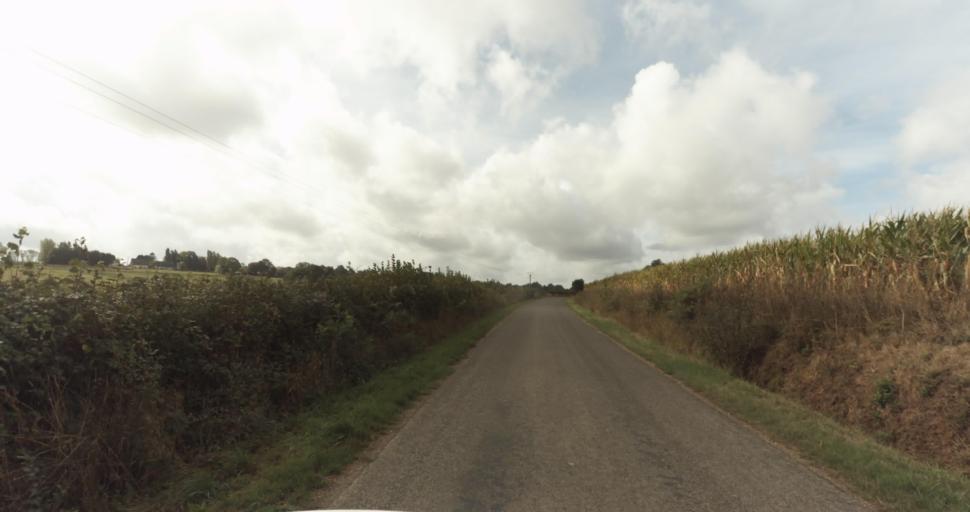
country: FR
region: Lower Normandy
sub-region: Departement de l'Orne
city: Gace
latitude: 48.8409
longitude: 0.3856
